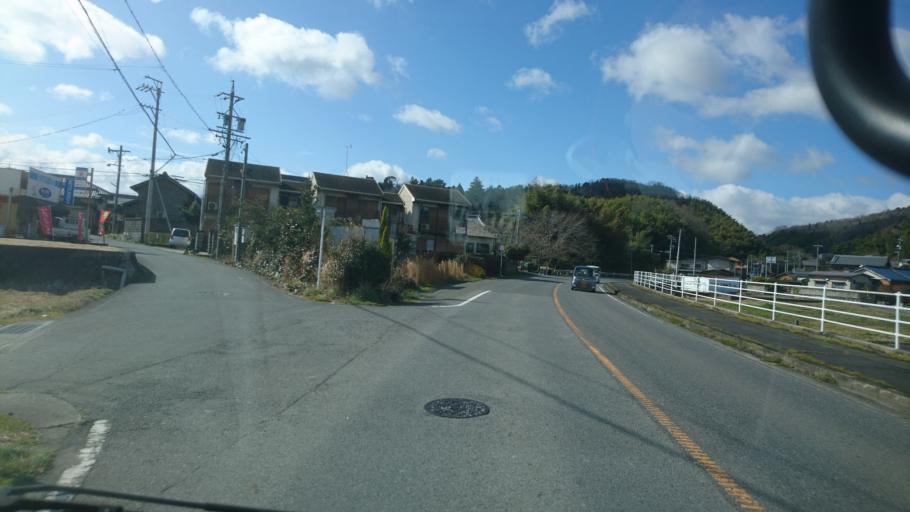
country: JP
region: Mie
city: Ueno-ebisumachi
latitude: 34.7672
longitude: 136.1047
